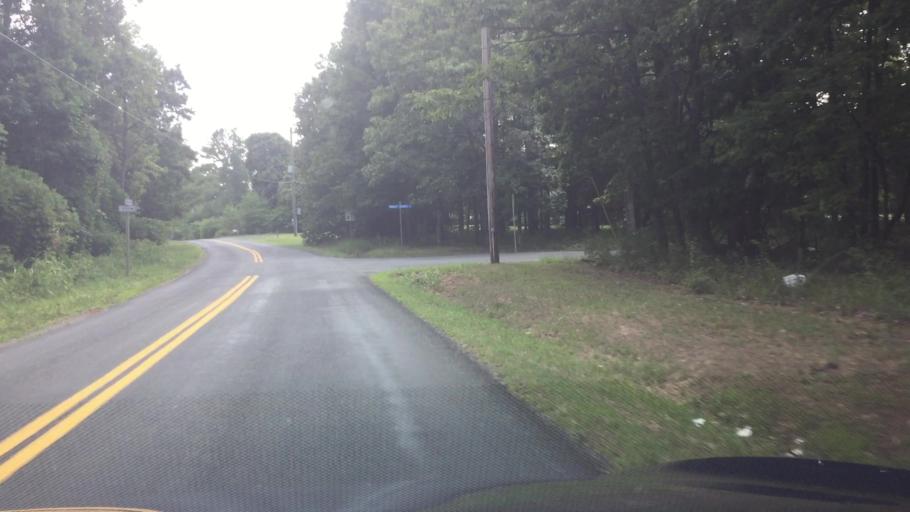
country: US
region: Virginia
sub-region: Appomattox County
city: Appomattox
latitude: 37.2952
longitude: -78.8510
